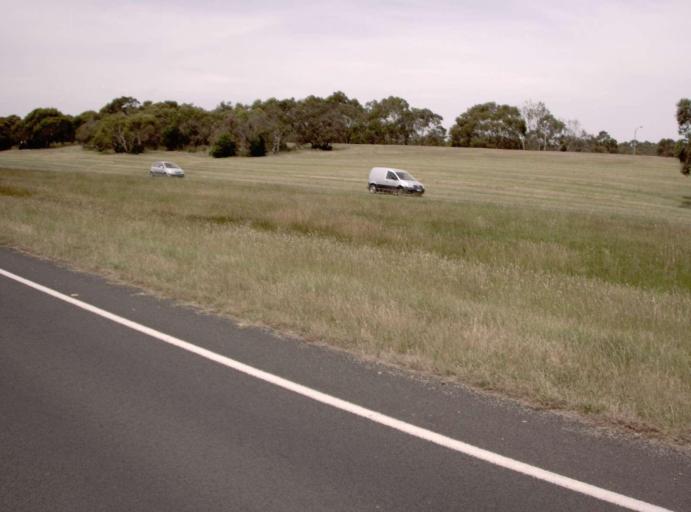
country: AU
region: Victoria
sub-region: Mornington Peninsula
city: Safety Beach
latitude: -38.3023
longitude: 145.0294
